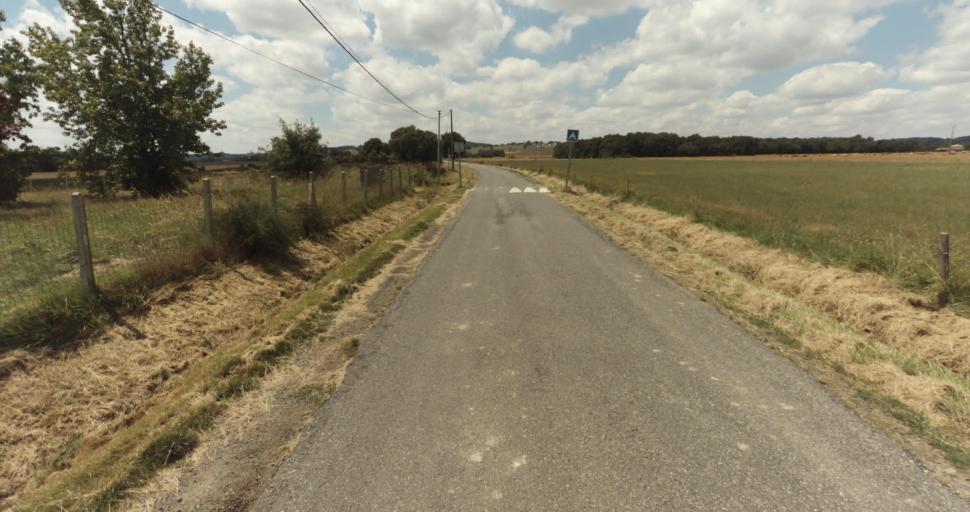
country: FR
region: Midi-Pyrenees
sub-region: Departement de la Haute-Garonne
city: Fontenilles
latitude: 43.5407
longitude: 1.1761
